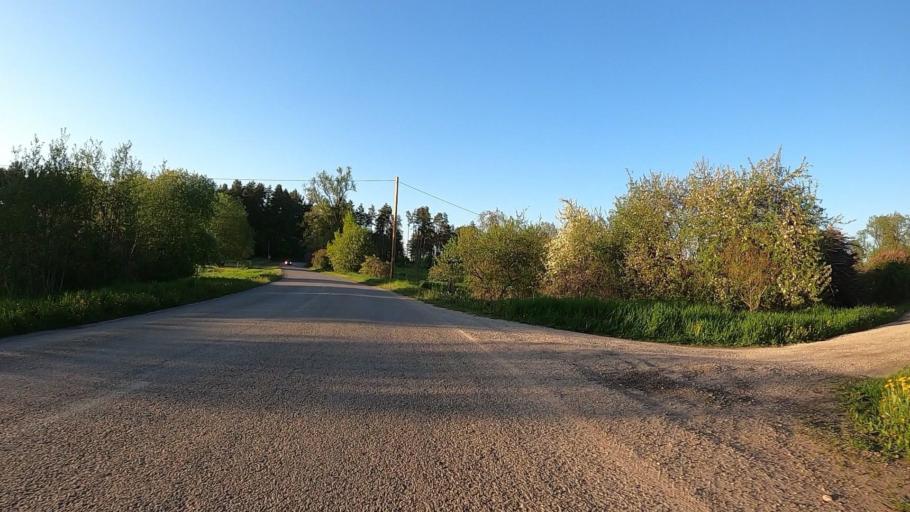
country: LV
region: Kekava
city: Kekava
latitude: 56.8188
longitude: 24.2234
